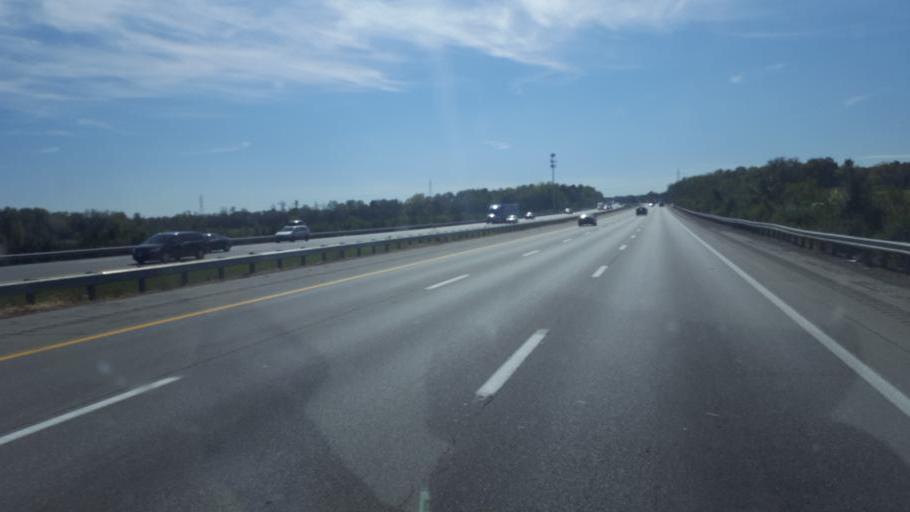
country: US
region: Ohio
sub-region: Franklin County
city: Westerville
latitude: 40.1723
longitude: -82.9588
